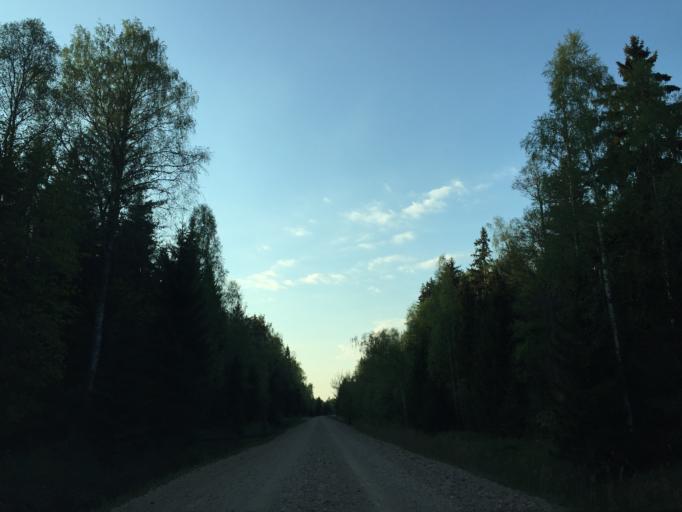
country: LV
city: Tireli
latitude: 56.8453
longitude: 23.6969
